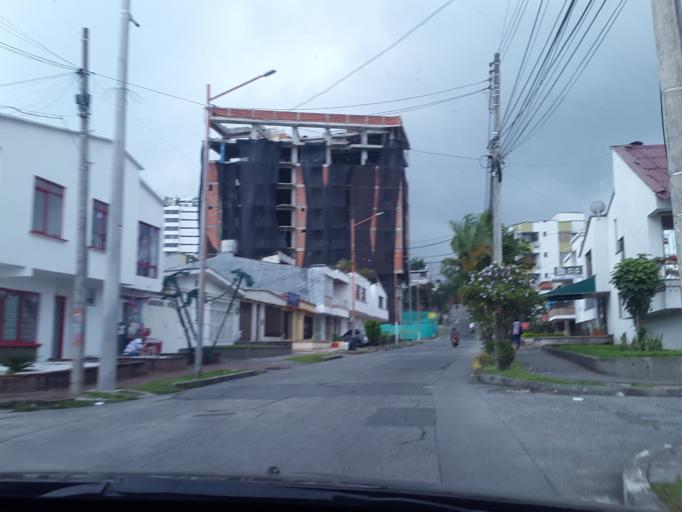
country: CO
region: Quindio
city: Armenia
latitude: 4.5467
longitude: -75.6640
